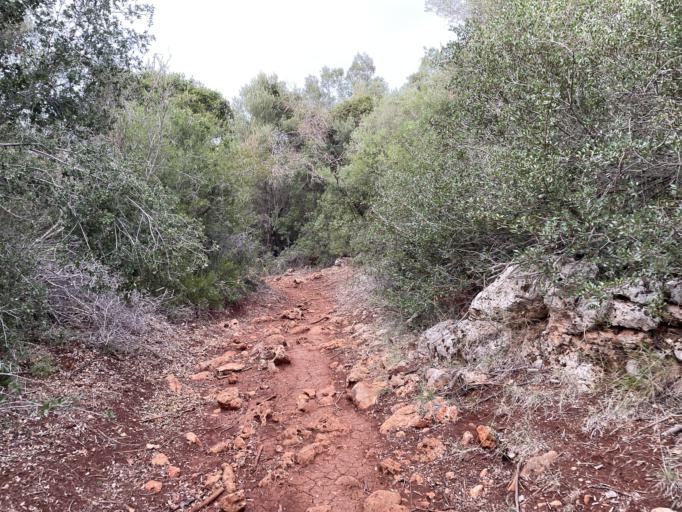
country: TR
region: Antalya
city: Kas
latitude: 36.1658
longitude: 29.6536
